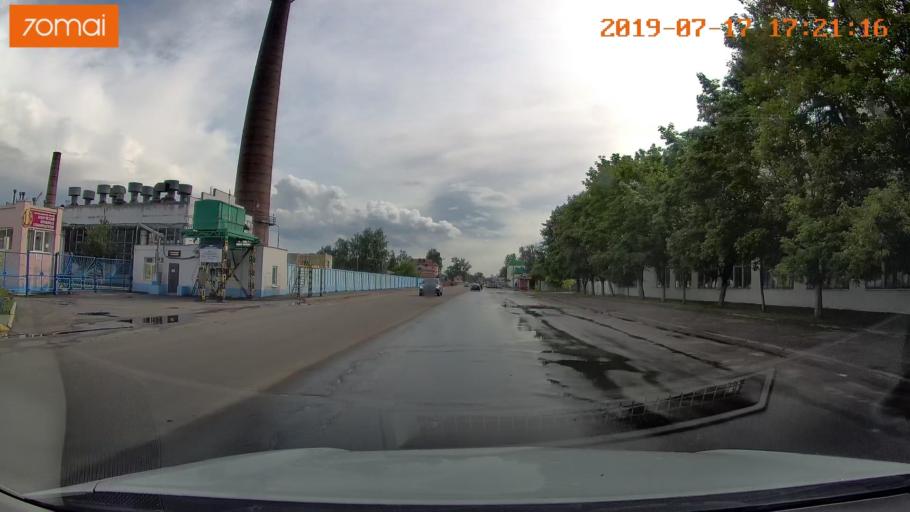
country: BY
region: Mogilev
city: Babruysk
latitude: 53.1490
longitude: 29.1800
